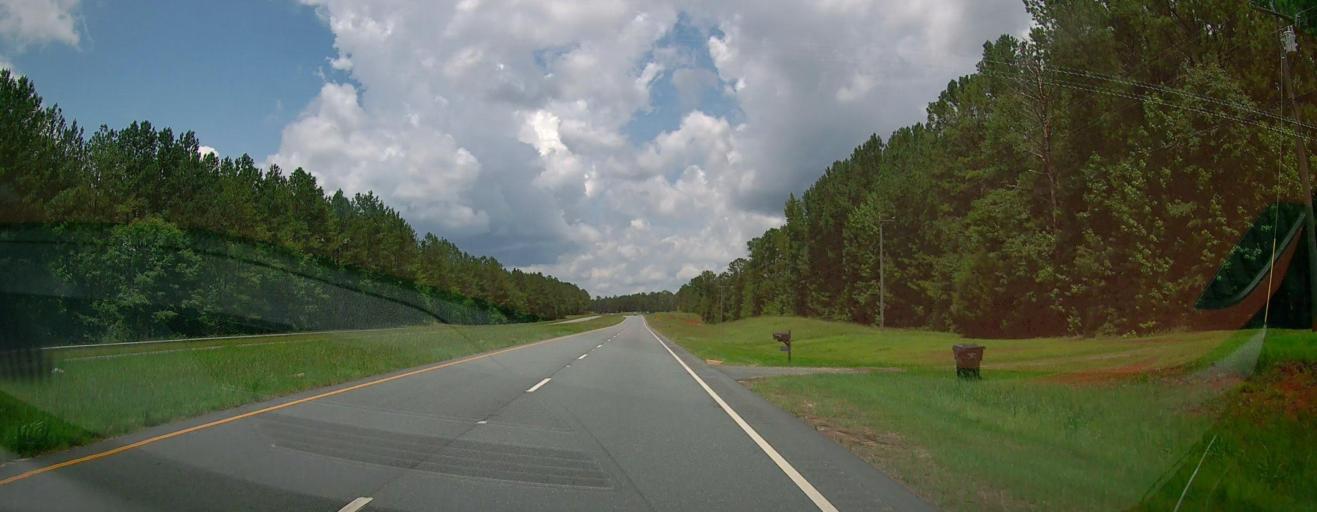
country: US
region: Georgia
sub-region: Upson County
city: Thomaston
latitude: 32.7998
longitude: -84.2733
